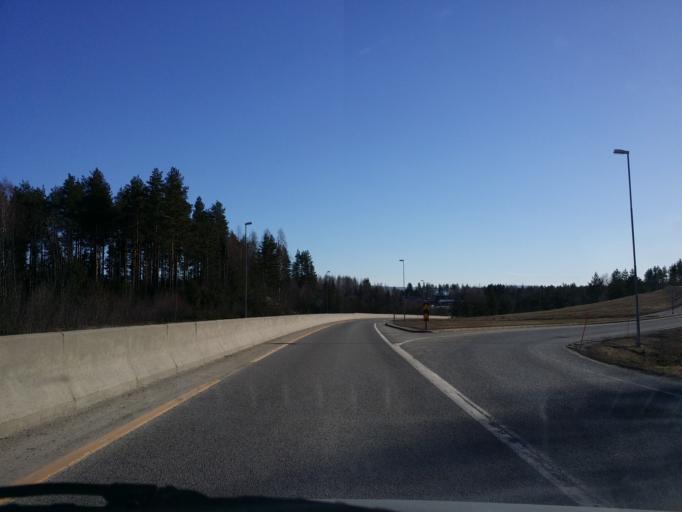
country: NO
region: Buskerud
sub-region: Ringerike
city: Honefoss
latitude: 60.2047
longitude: 10.2590
